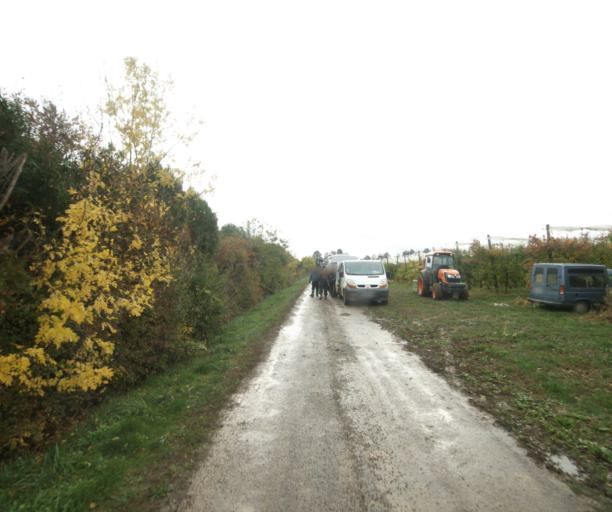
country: FR
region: Rhone-Alpes
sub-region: Departement de l'Ain
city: Pont-de-Vaux
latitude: 46.4832
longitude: 4.8848
